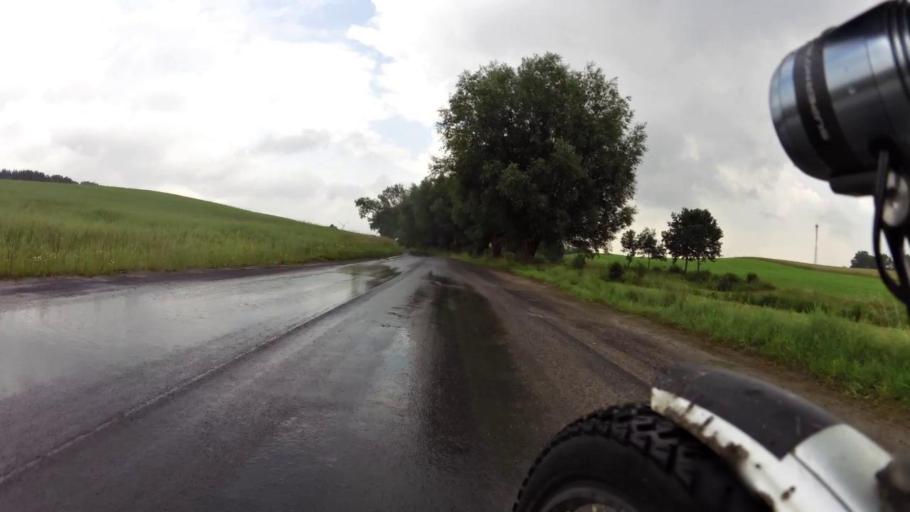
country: PL
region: West Pomeranian Voivodeship
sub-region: Powiat swidwinski
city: Swidwin
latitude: 53.7245
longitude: 15.6954
